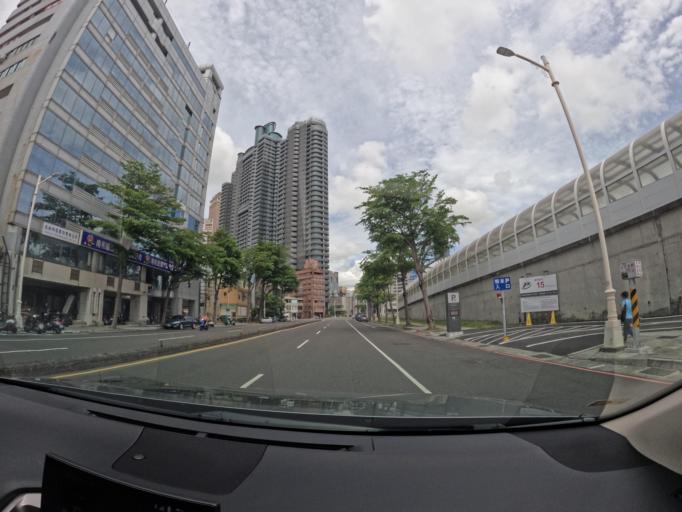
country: TW
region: Kaohsiung
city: Kaohsiung
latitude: 22.6197
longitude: 120.2919
